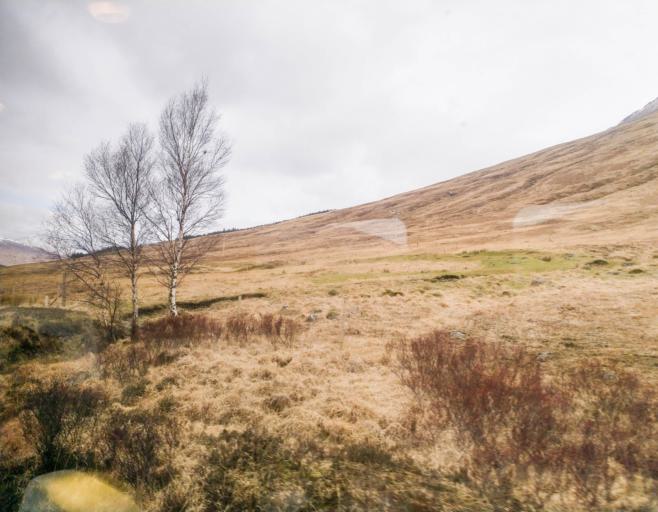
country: GB
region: Scotland
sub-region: Argyll and Bute
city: Garelochhead
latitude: 56.4982
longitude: -4.7475
